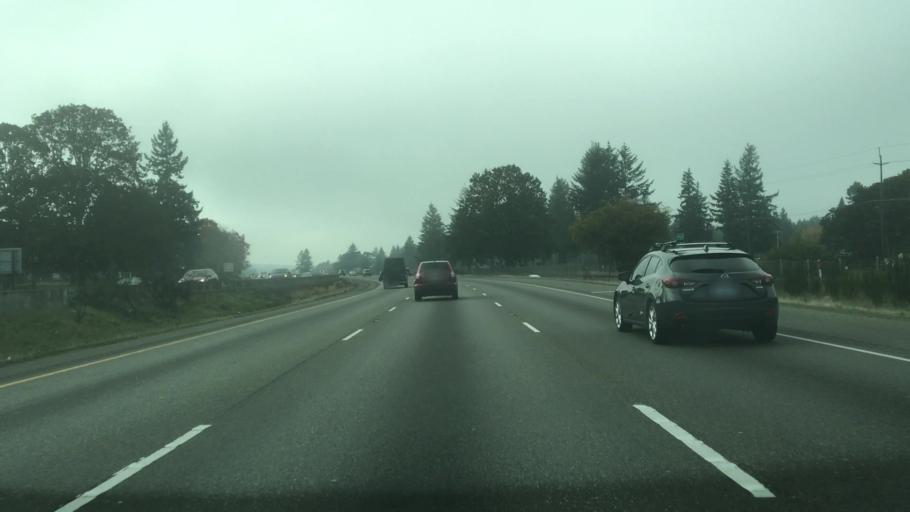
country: US
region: Washington
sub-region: Pierce County
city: DuPont
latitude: 47.1007
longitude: -122.6058
